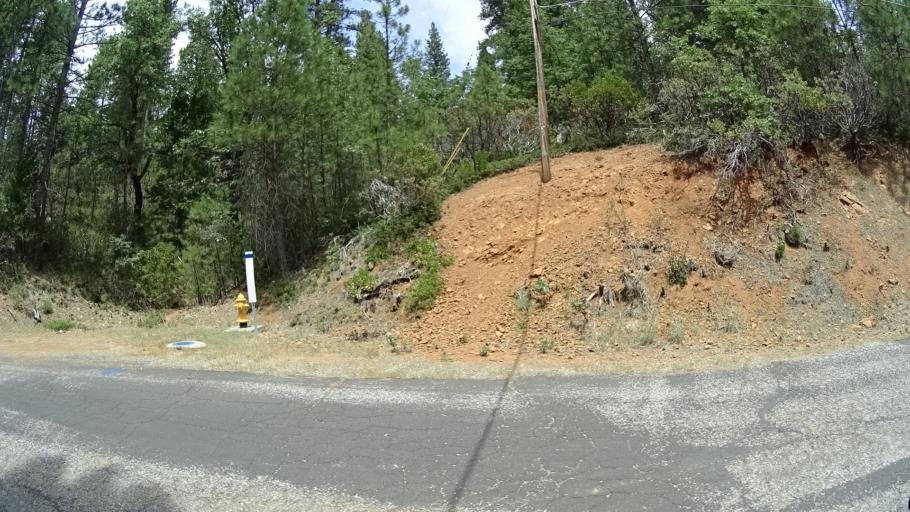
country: US
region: California
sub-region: Calaveras County
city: Arnold
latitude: 38.2348
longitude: -120.3484
